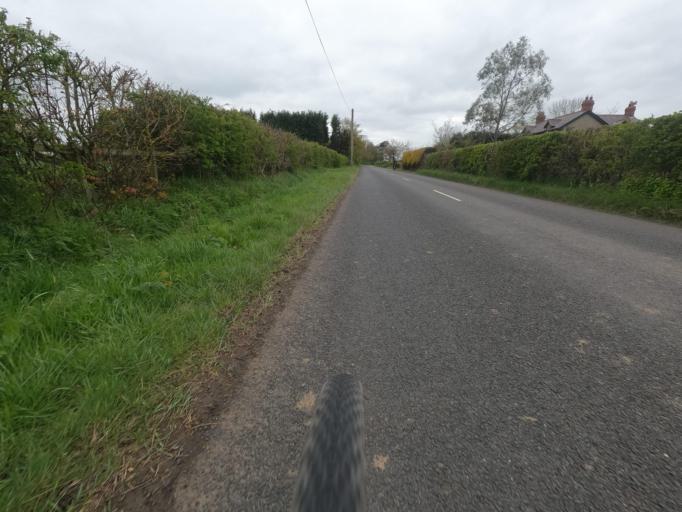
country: GB
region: England
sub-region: Northumberland
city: Darras Hall
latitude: 55.0475
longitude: -1.7975
